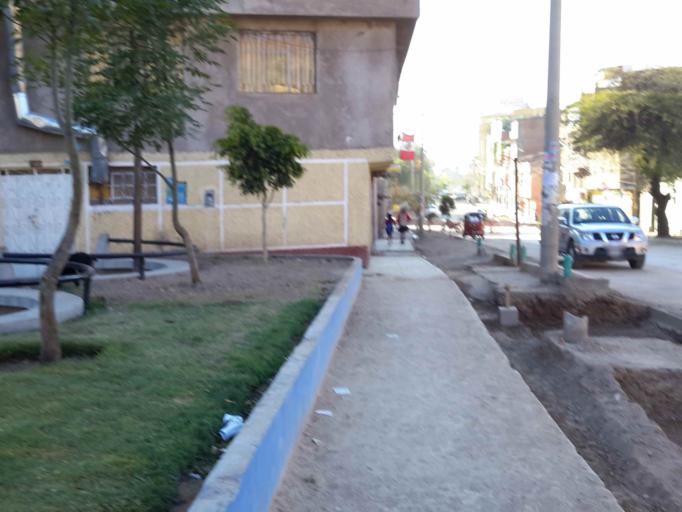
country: PE
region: Ayacucho
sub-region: Provincia de Huamanga
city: Ayacucho
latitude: -13.1548
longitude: -74.2247
